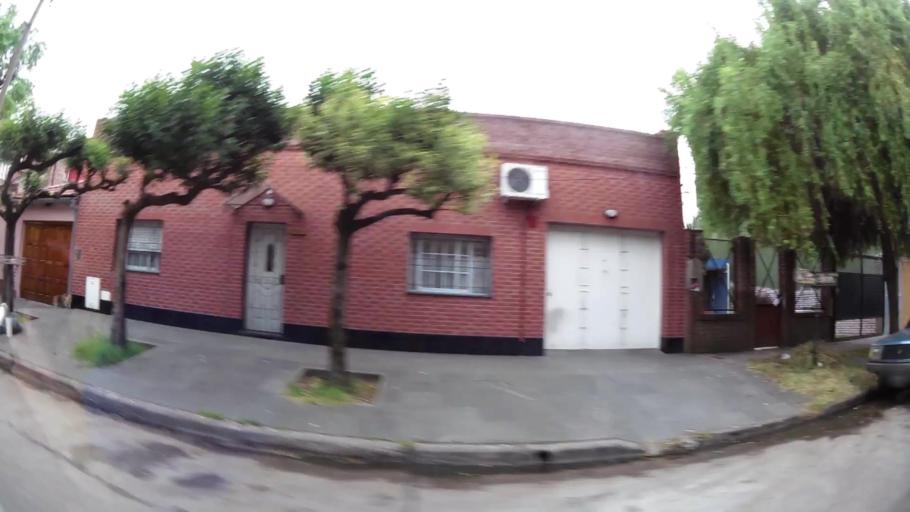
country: AR
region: Buenos Aires F.D.
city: Villa Lugano
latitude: -34.7081
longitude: -58.5162
